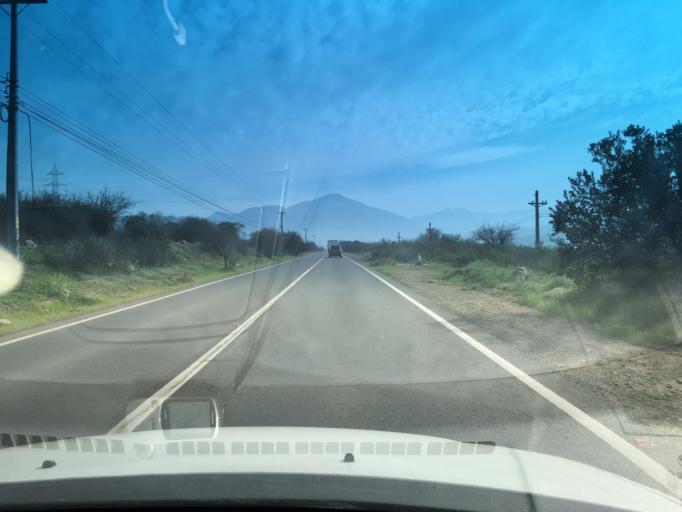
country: CL
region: Santiago Metropolitan
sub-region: Provincia de Chacabuco
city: Lampa
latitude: -33.1345
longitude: -70.9193
